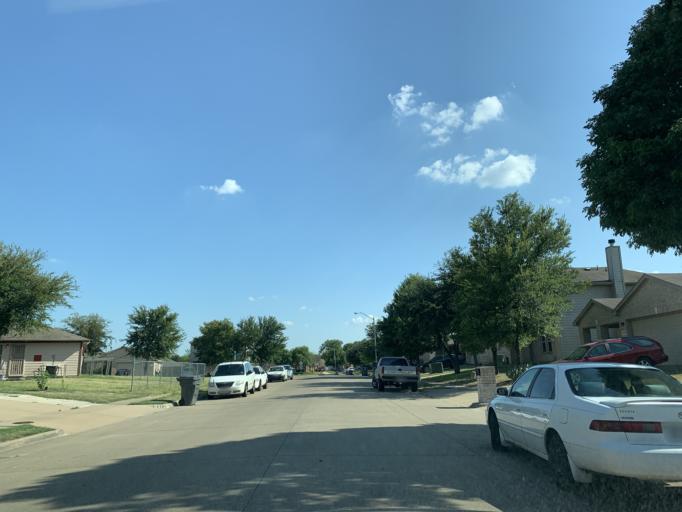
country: US
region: Texas
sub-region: Dallas County
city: Hutchins
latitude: 32.6668
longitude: -96.7692
